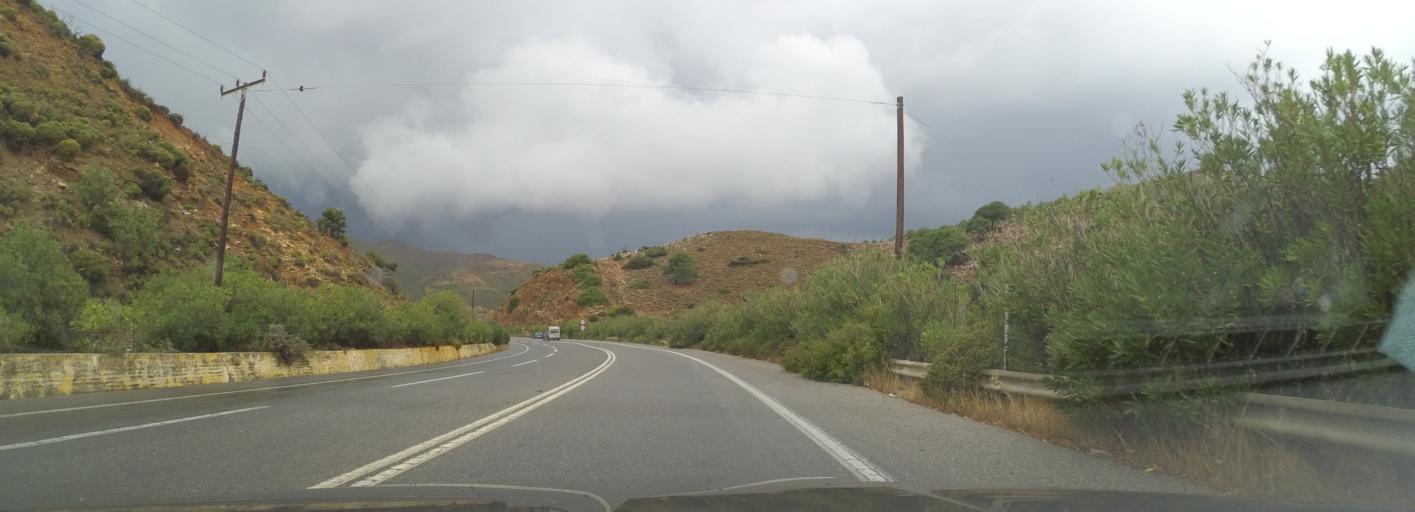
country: GR
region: Crete
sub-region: Nomos Rethymnis
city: Anogeia
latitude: 35.3928
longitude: 24.9270
